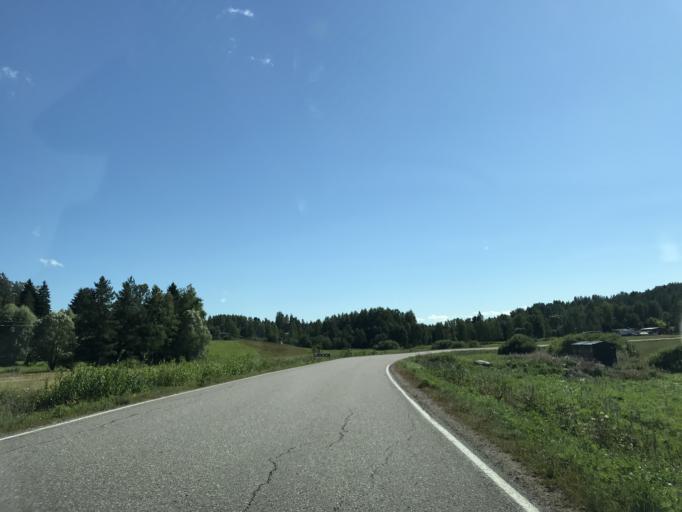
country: FI
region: Paijanne Tavastia
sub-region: Lahti
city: Orimattila
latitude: 60.8039
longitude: 25.6921
